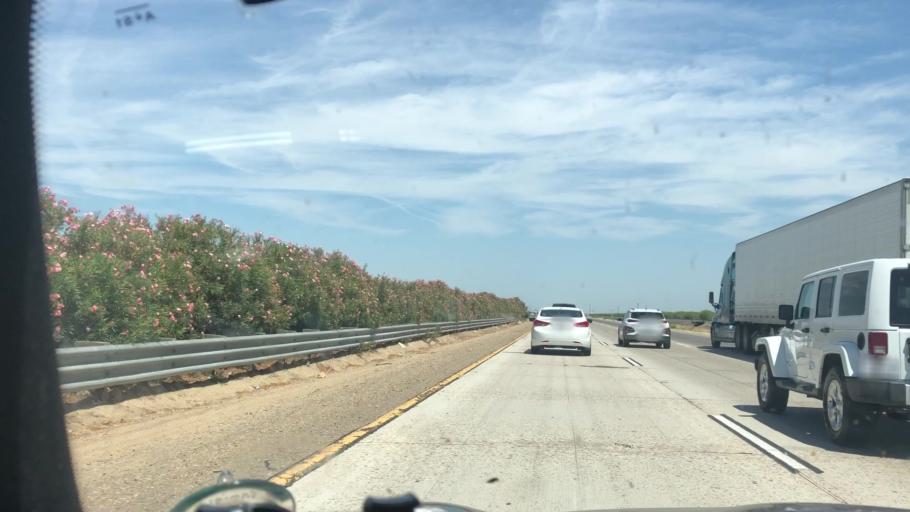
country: US
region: California
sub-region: Kern County
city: McFarland
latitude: 35.6176
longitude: -119.2129
